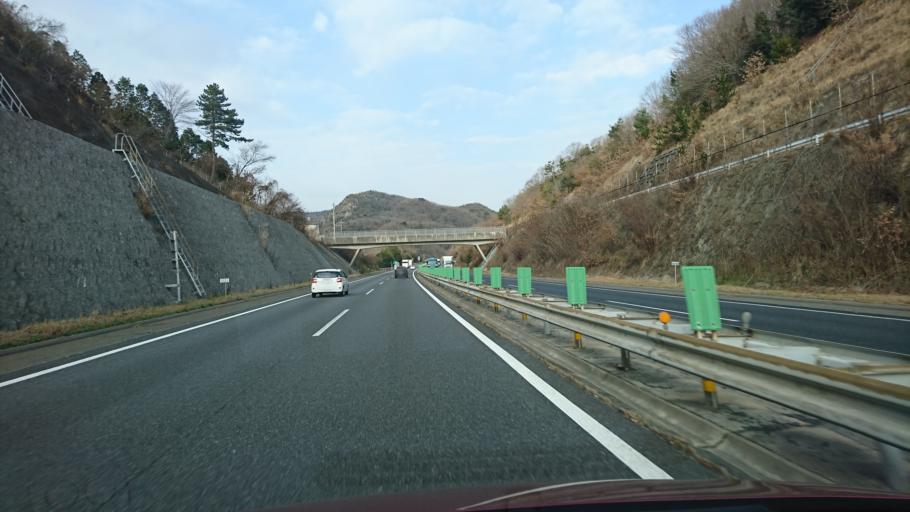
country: JP
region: Hyogo
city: Kariya
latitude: 34.7815
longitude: 134.2241
